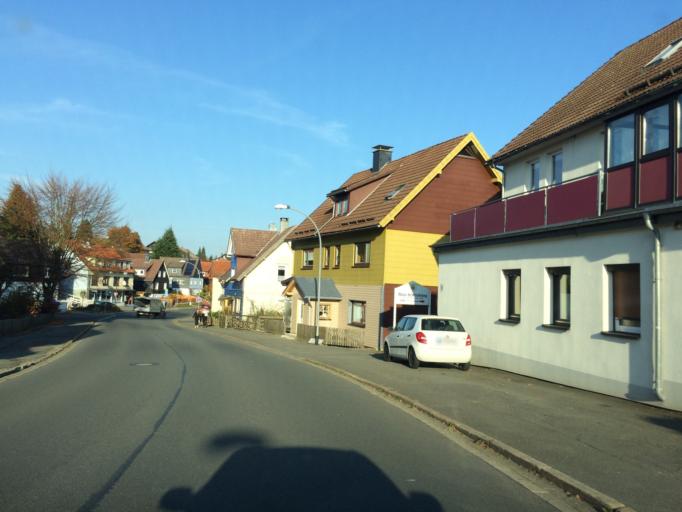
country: DE
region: Lower Saxony
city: Braunlage
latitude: 51.7203
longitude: 10.6051
